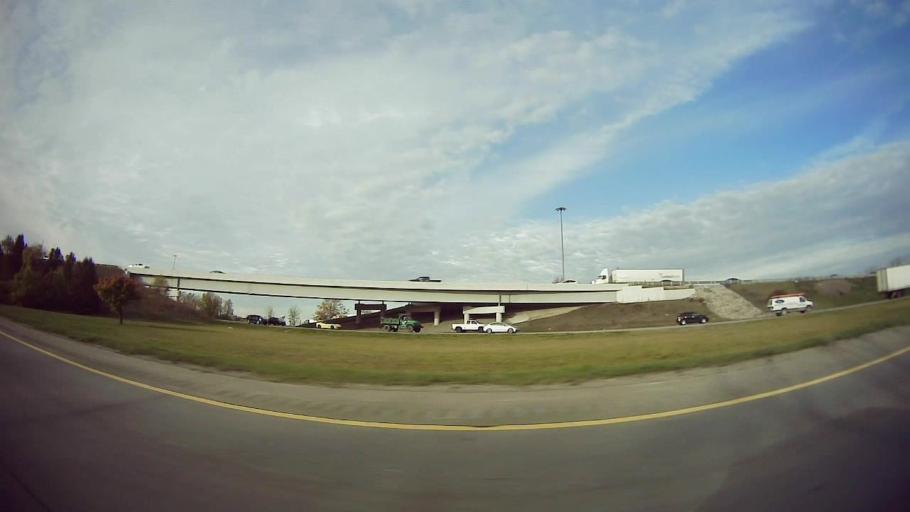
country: US
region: Michigan
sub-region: Wayne County
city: Plymouth
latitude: 42.3914
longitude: -83.4332
